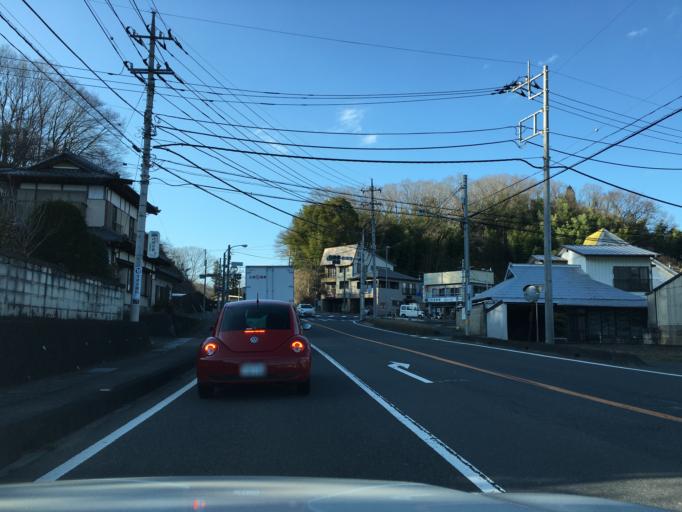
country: JP
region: Ibaraki
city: Daigo
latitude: 36.7579
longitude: 140.3823
